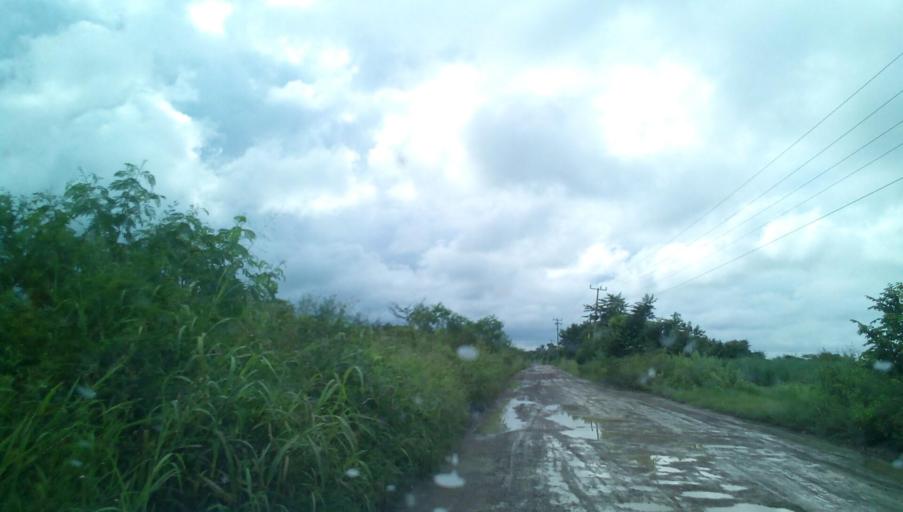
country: MX
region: Veracruz
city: Panuco
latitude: 21.8488
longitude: -98.1409
